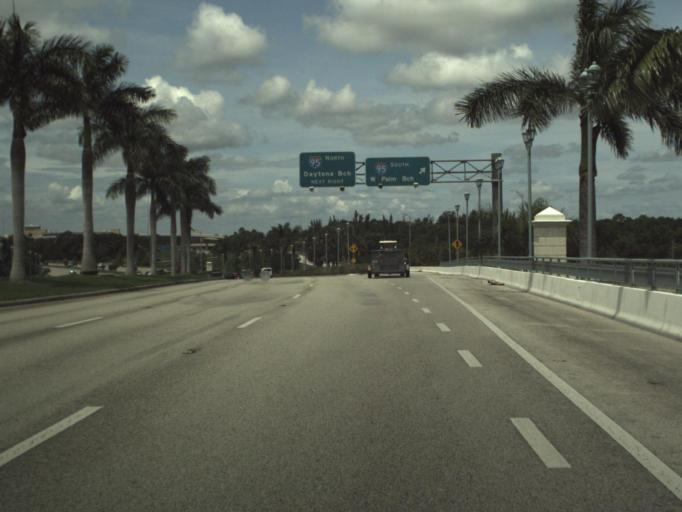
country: US
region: Florida
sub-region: Palm Beach County
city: North Palm Beach
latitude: 26.8436
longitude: -80.0966
